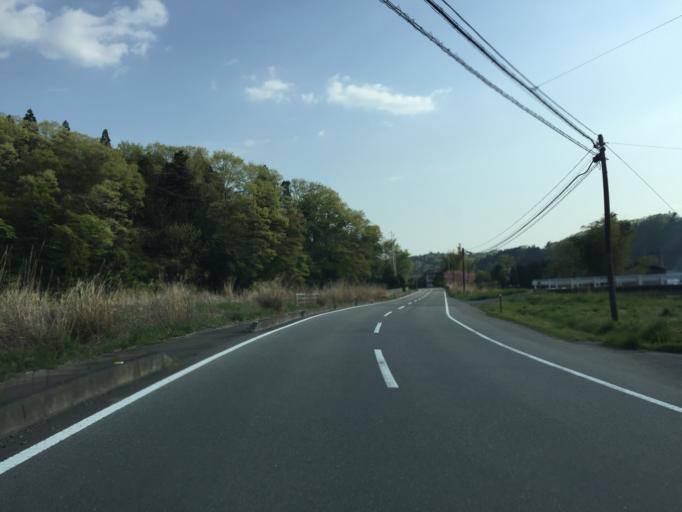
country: JP
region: Fukushima
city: Iwaki
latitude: 36.9809
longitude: 140.8015
